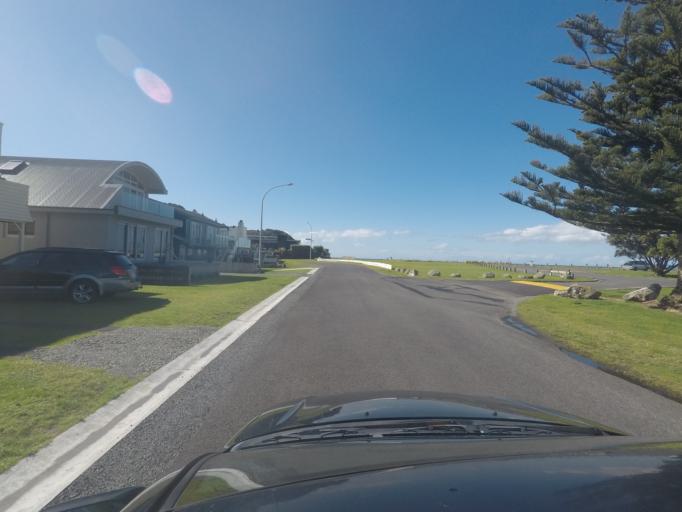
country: NZ
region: Bay of Plenty
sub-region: Western Bay of Plenty District
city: Waihi Beach
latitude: -37.4006
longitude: 175.9393
